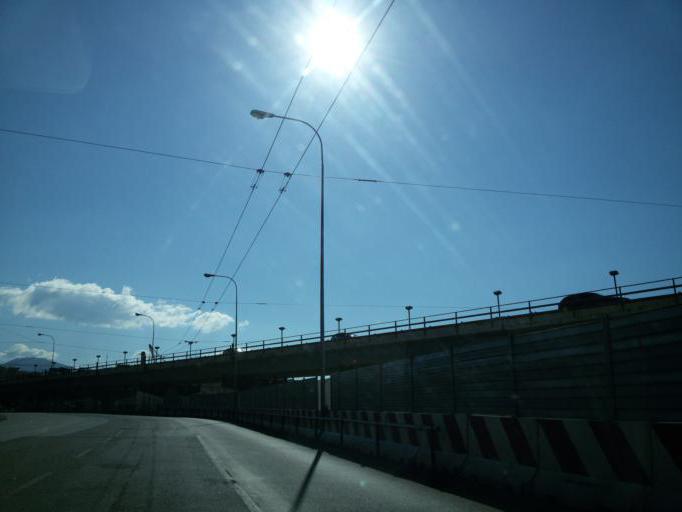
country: IT
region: Liguria
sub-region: Provincia di Genova
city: San Teodoro
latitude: 44.4150
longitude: 8.9154
